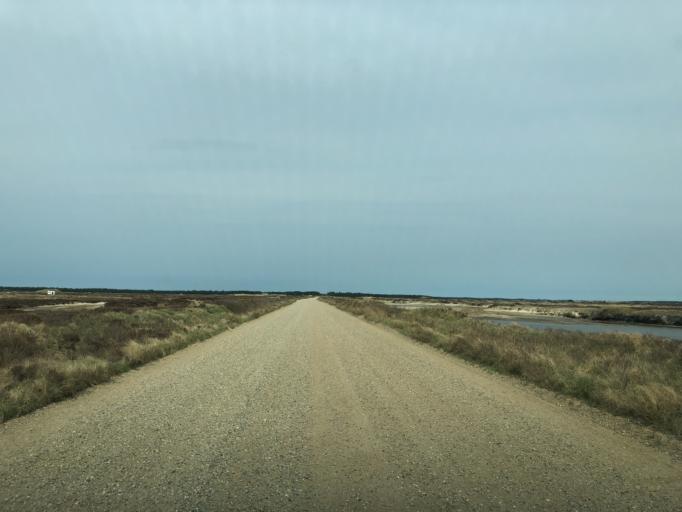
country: DK
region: South Denmark
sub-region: Varde Kommune
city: Oksbol
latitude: 55.5854
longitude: 8.1464
